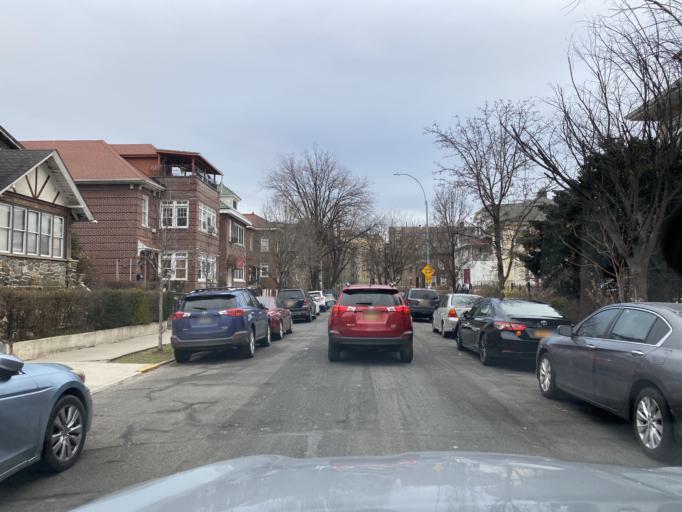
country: US
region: New York
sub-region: New York County
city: Inwood
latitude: 40.8715
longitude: -73.9012
